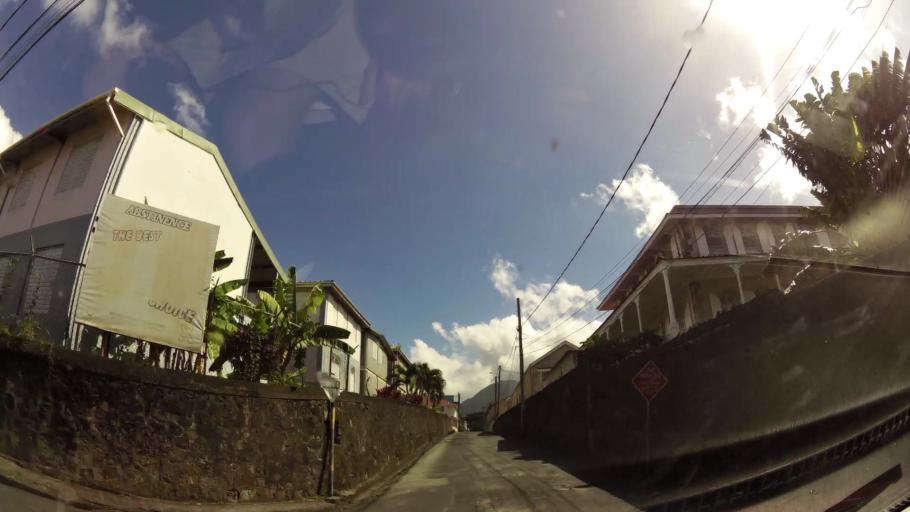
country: DM
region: Saint George
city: Roseau
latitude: 15.2984
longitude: -61.3851
